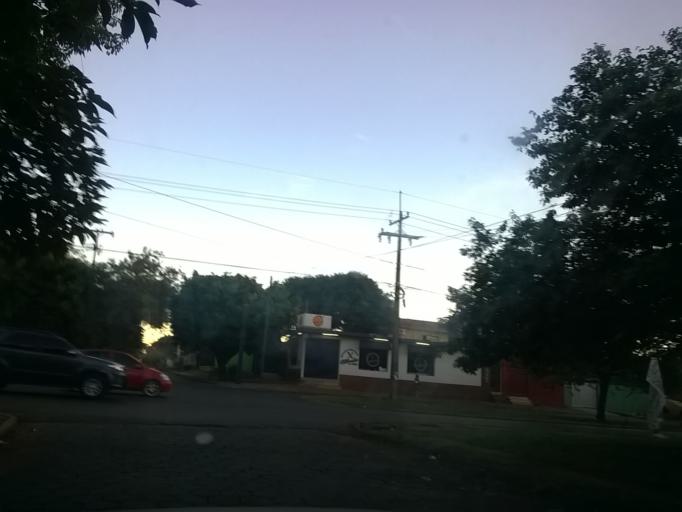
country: PY
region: Alto Parana
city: Presidente Franco
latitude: -25.5359
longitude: -54.6299
